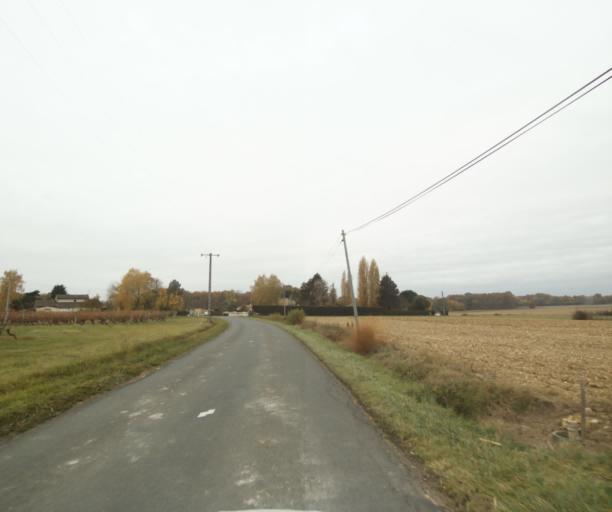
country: FR
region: Poitou-Charentes
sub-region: Departement de la Charente-Maritime
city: Chermignac
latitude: 45.7191
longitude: -0.6952
